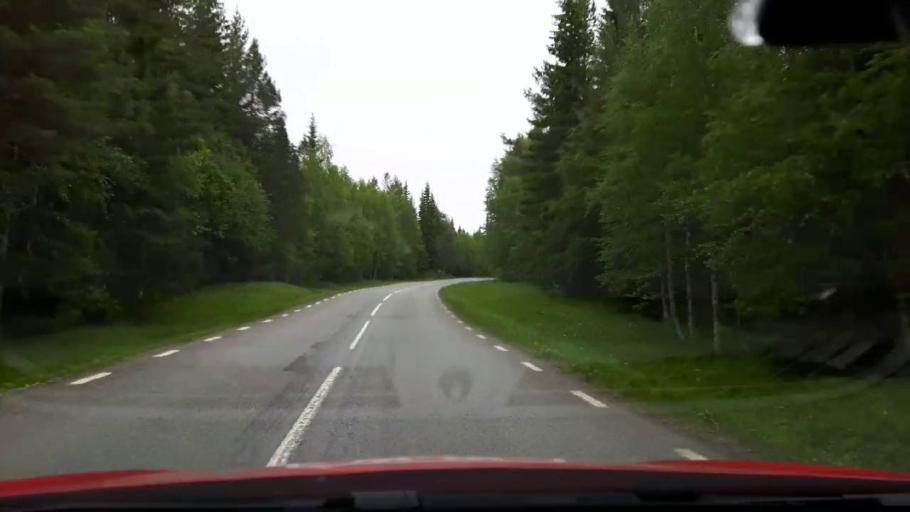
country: SE
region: Jaemtland
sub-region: Stroemsunds Kommun
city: Stroemsund
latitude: 63.4782
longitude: 15.4451
